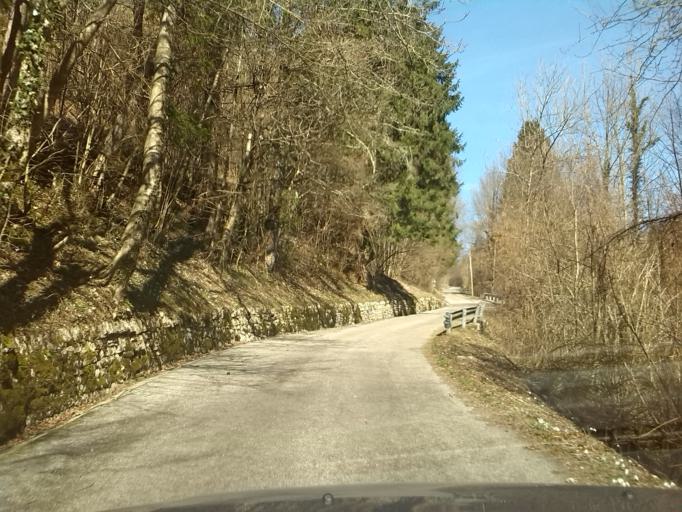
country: IT
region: Friuli Venezia Giulia
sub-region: Provincia di Udine
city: Clodig
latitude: 46.1854
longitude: 13.5827
